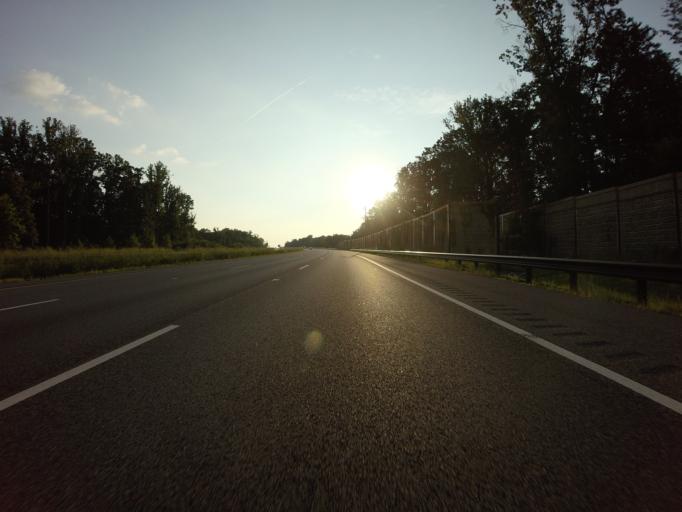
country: US
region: Maryland
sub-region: Montgomery County
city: Colesville
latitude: 39.0896
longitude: -76.9866
